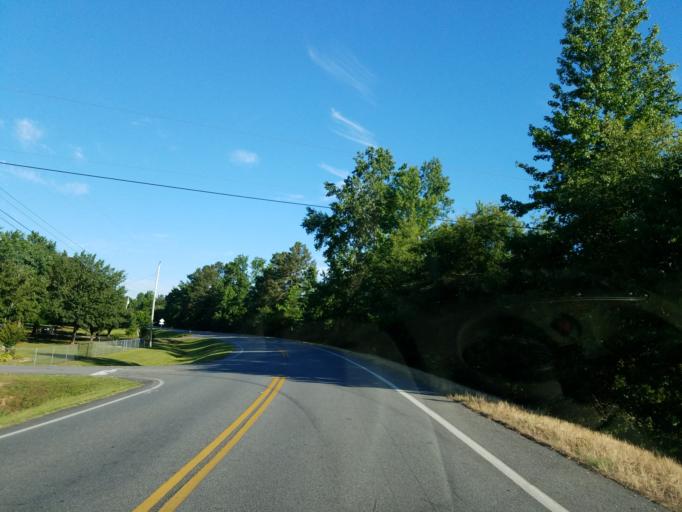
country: US
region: Georgia
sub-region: Gordon County
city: Calhoun
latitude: 34.5450
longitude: -85.0023
